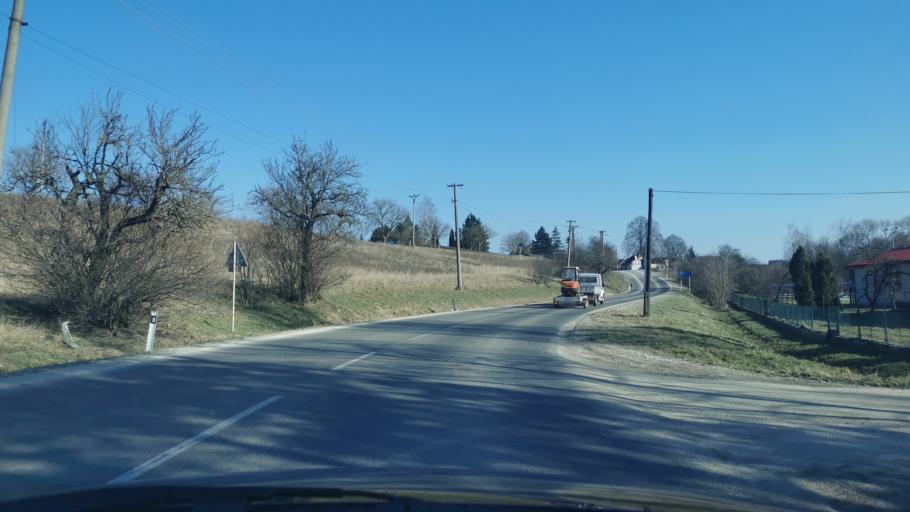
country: SK
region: Trenciansky
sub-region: Okres Myjava
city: Myjava
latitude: 48.7499
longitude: 17.5229
